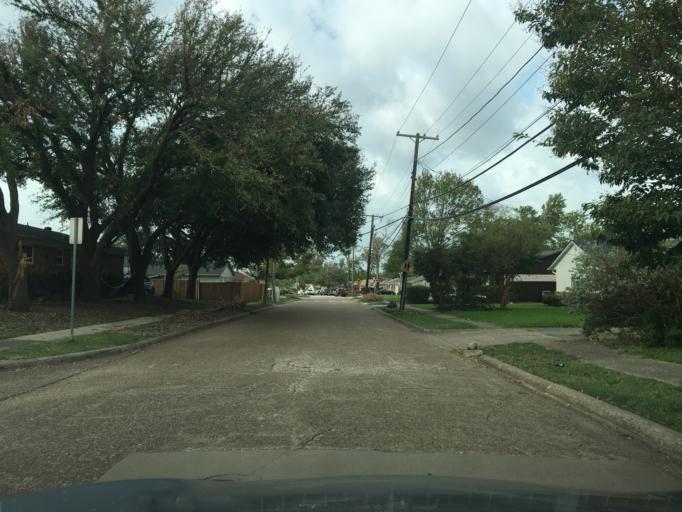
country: US
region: Texas
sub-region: Dallas County
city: Richardson
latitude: 32.9034
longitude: -96.7572
